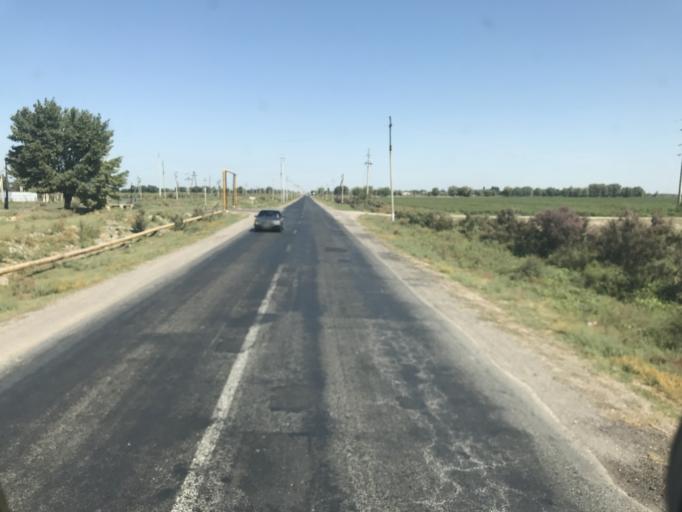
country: KZ
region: Ongtustik Qazaqstan
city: Ilyich
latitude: 40.8783
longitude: 68.4881
